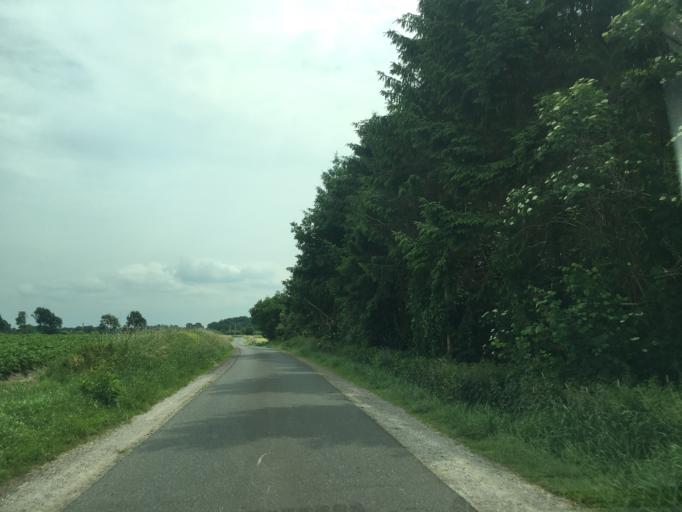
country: DE
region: North Rhine-Westphalia
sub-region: Regierungsbezirk Munster
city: Muenster
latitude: 52.0257
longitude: 7.6260
